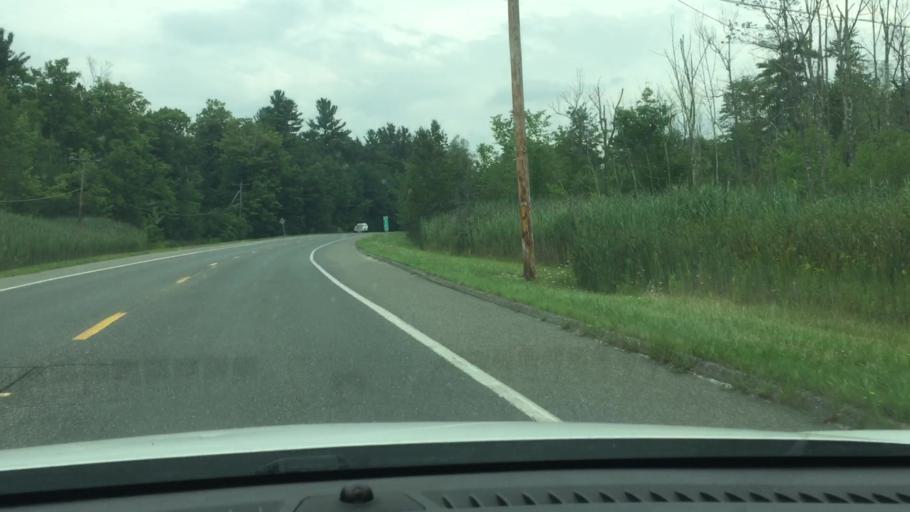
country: US
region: Massachusetts
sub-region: Berkshire County
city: Lenox
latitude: 42.3281
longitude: -73.2880
